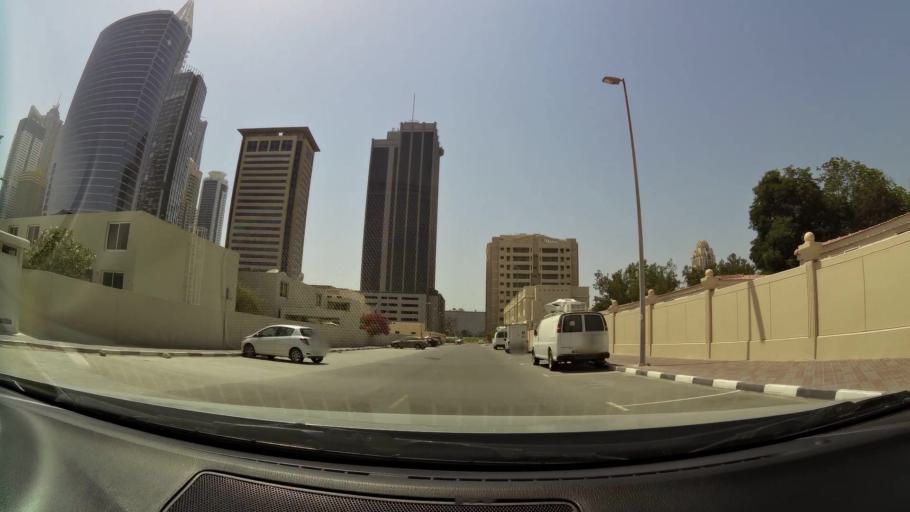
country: AE
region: Dubai
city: Dubai
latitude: 25.0897
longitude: 55.1553
